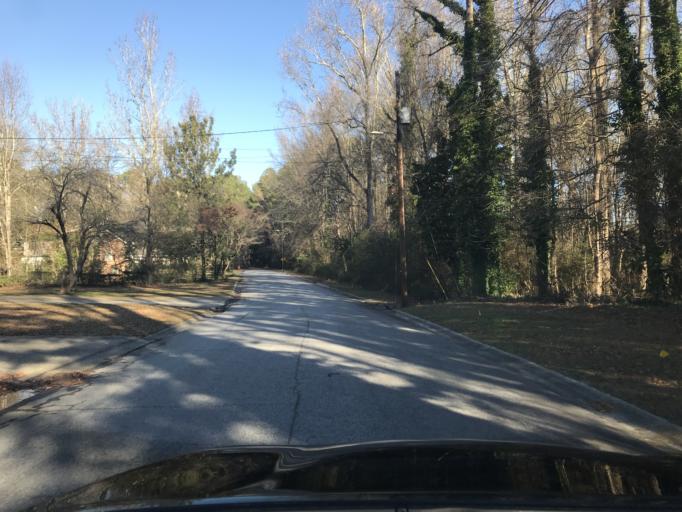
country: US
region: Georgia
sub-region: Clayton County
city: Morrow
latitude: 33.5655
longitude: -84.3630
